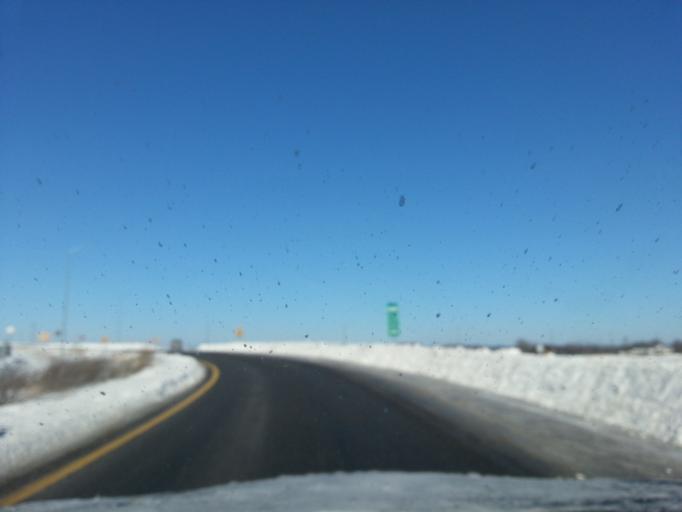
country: CA
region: Ontario
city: Arnprior
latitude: 45.3632
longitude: -76.2320
